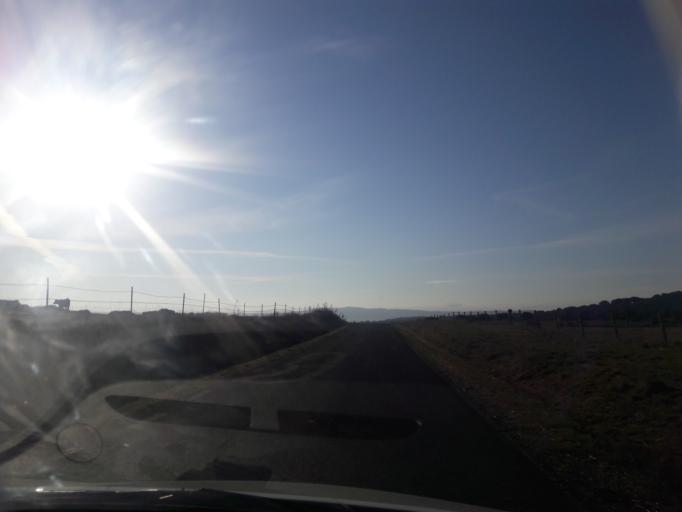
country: ES
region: Castille and Leon
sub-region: Provincia de Salamanca
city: Montejo
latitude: 40.6262
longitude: -5.6148
